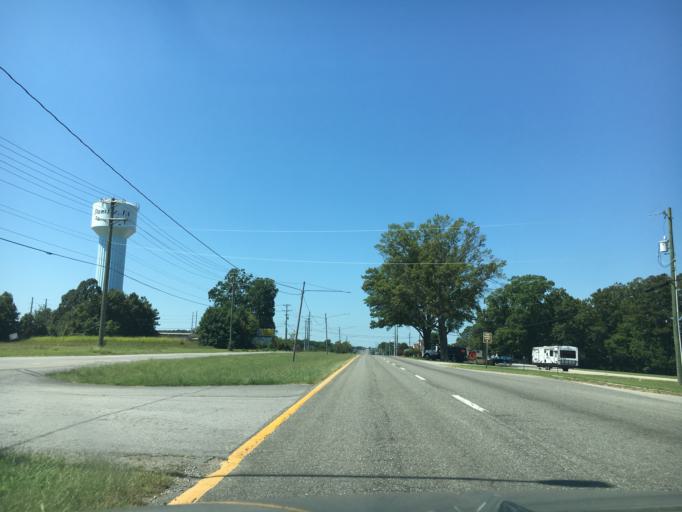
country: US
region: Virginia
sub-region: City of Danville
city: Danville
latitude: 36.5809
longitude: -79.3093
